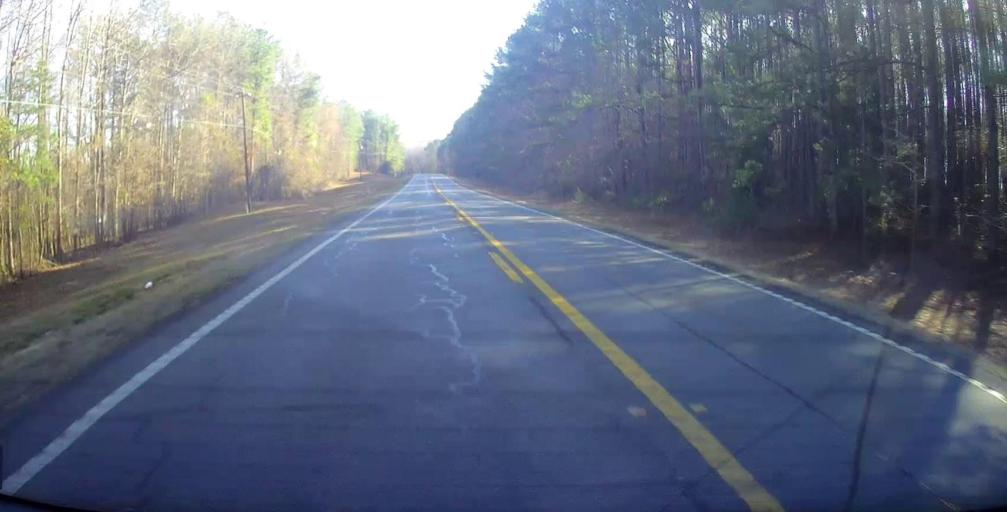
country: US
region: Georgia
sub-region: Talbot County
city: Talbotton
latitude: 32.7193
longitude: -84.5565
